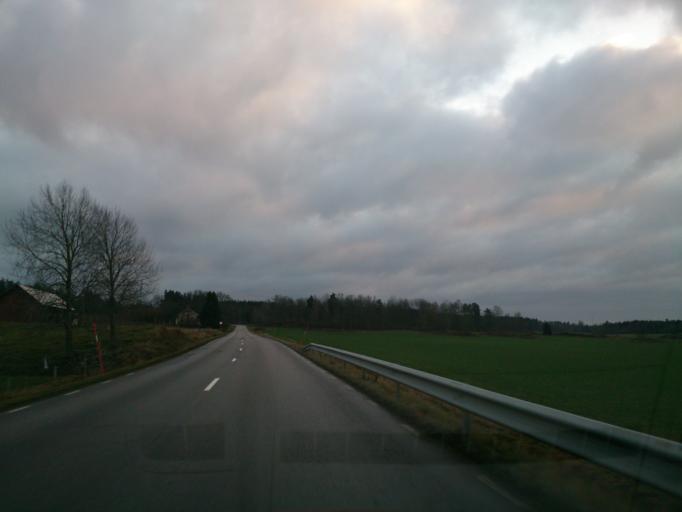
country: SE
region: OEstergoetland
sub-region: Atvidabergs Kommun
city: Atvidaberg
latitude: 58.3667
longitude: 16.0240
